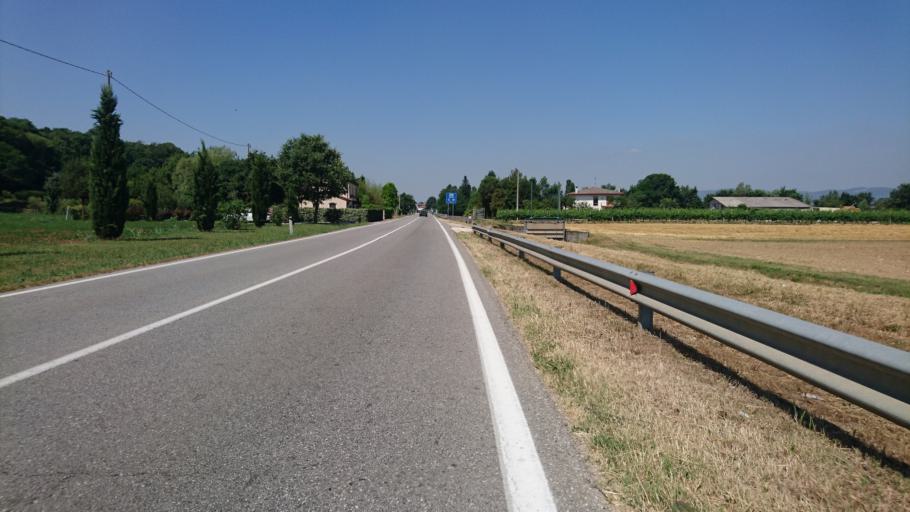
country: IT
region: Veneto
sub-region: Provincia di Padova
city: Bastia
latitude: 45.3940
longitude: 11.6714
